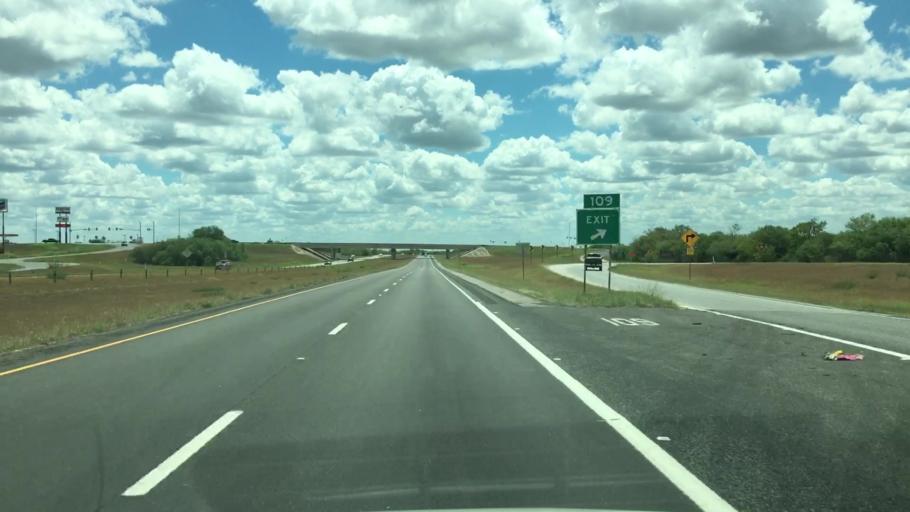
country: US
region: Texas
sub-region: Atascosa County
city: Pleasanton
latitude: 28.9979
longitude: -98.4314
